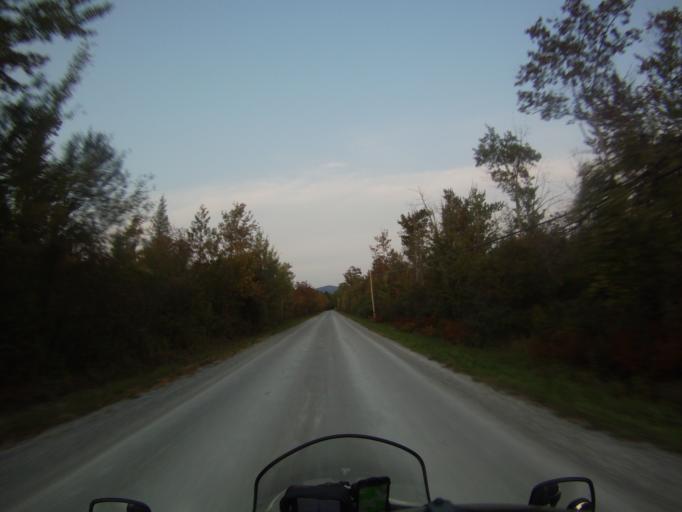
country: US
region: Vermont
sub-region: Rutland County
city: Brandon
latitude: 43.7848
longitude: -73.1220
